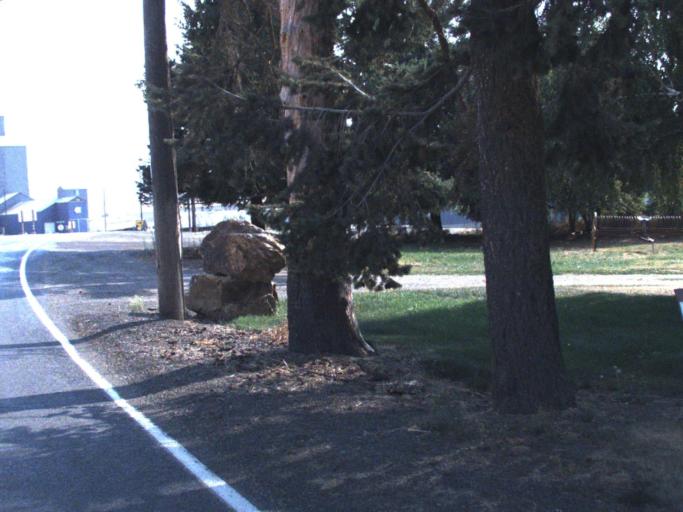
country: US
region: Idaho
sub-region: Benewah County
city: Plummer
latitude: 47.2398
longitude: -117.0426
